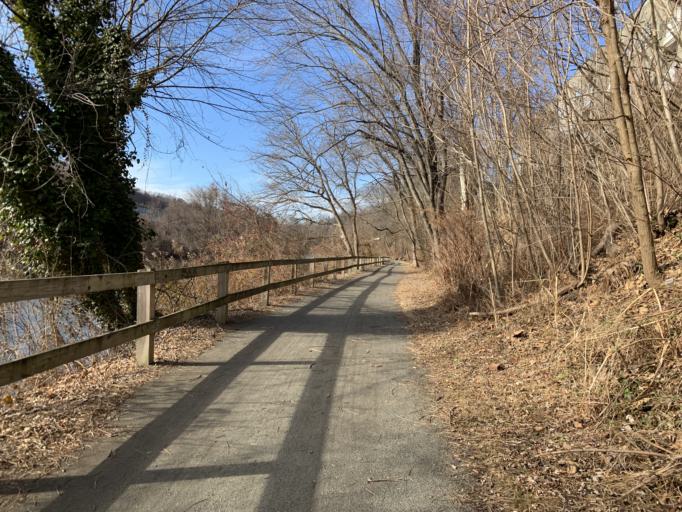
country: US
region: Pennsylvania
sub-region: Montgomery County
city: Bala-Cynwyd
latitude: 40.0348
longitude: -75.2374
